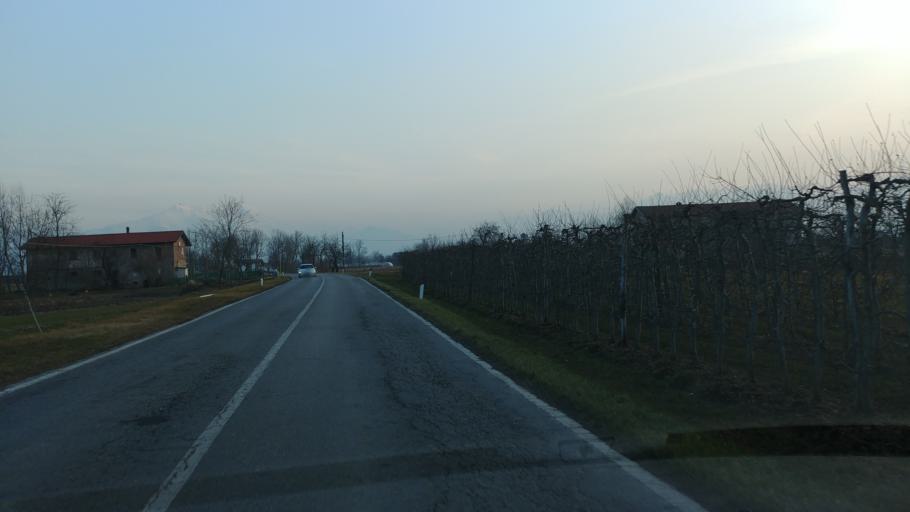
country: IT
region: Piedmont
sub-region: Provincia di Cuneo
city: Roata Rossi
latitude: 44.4214
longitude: 7.5076
